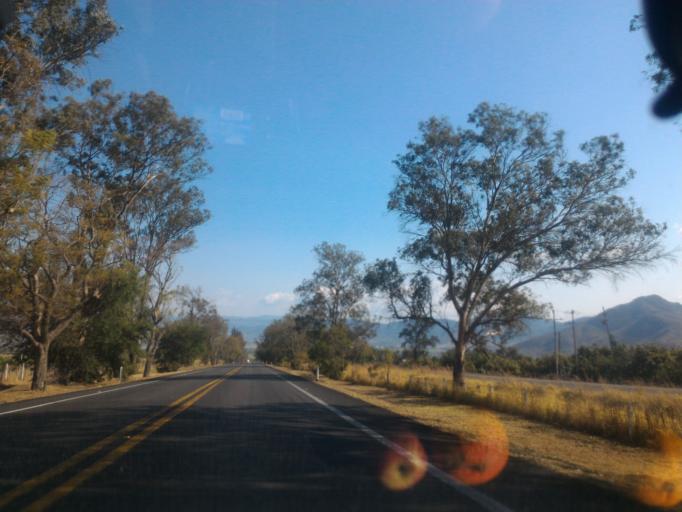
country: MX
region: Jalisco
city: Tuxpan
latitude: 19.5462
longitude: -103.4305
